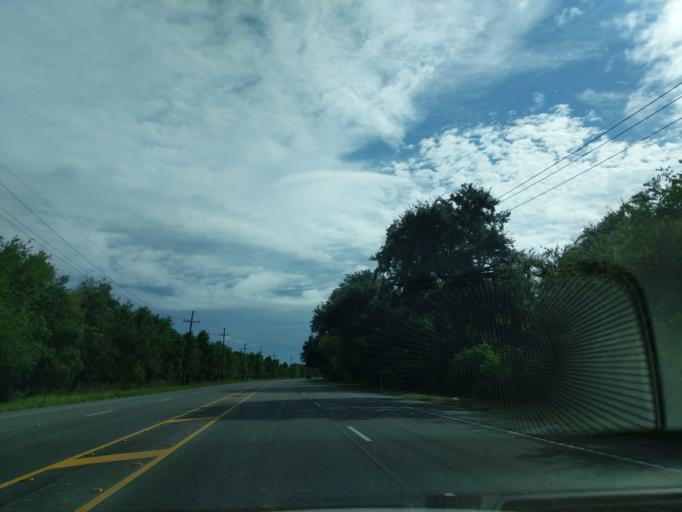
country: US
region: Louisiana
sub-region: Saint Bernard Parish
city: Meraux
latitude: 30.0680
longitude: -89.8643
